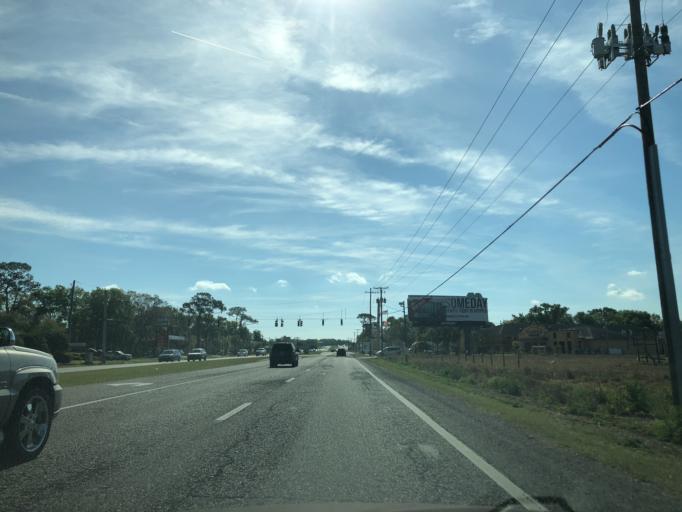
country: US
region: Florida
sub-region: Orange County
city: Apopka
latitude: 28.6867
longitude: -81.5373
